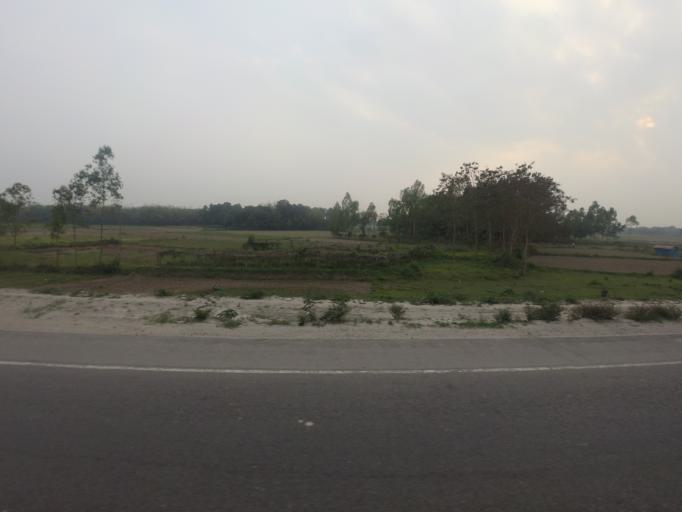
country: BD
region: Dhaka
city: Tangail
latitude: 24.1807
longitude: 90.0068
